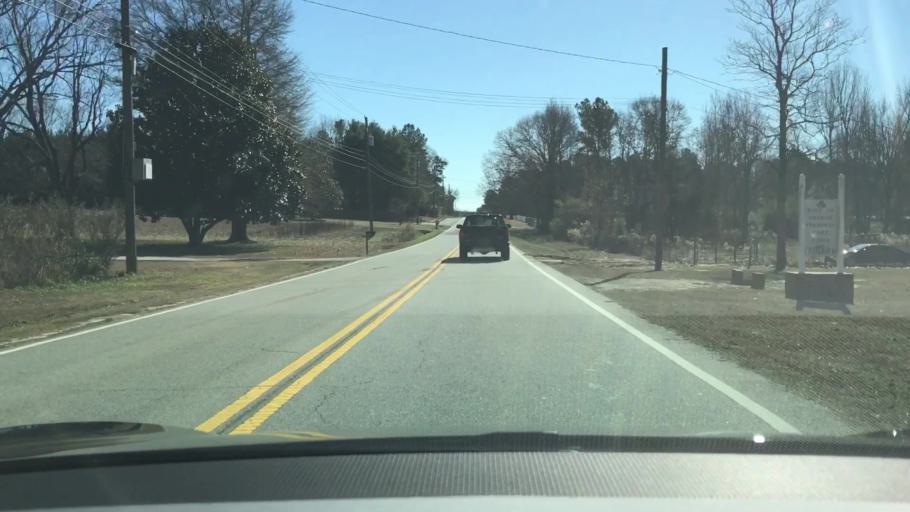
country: US
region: Georgia
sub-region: Gwinnett County
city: Dacula
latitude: 33.9670
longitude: -83.8868
